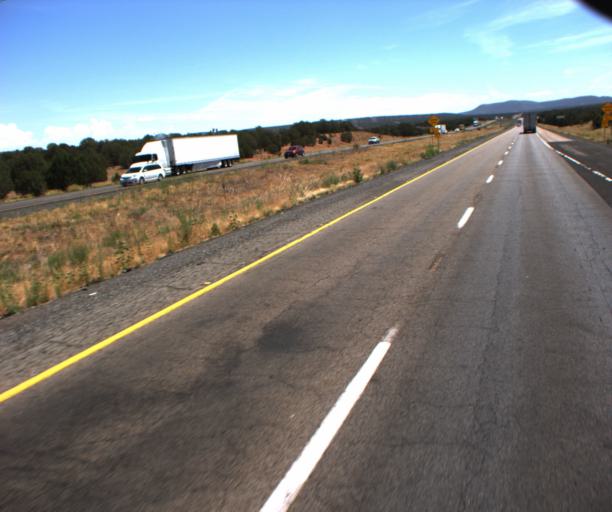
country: US
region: Arizona
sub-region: Mohave County
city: Peach Springs
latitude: 35.1907
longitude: -113.3589
